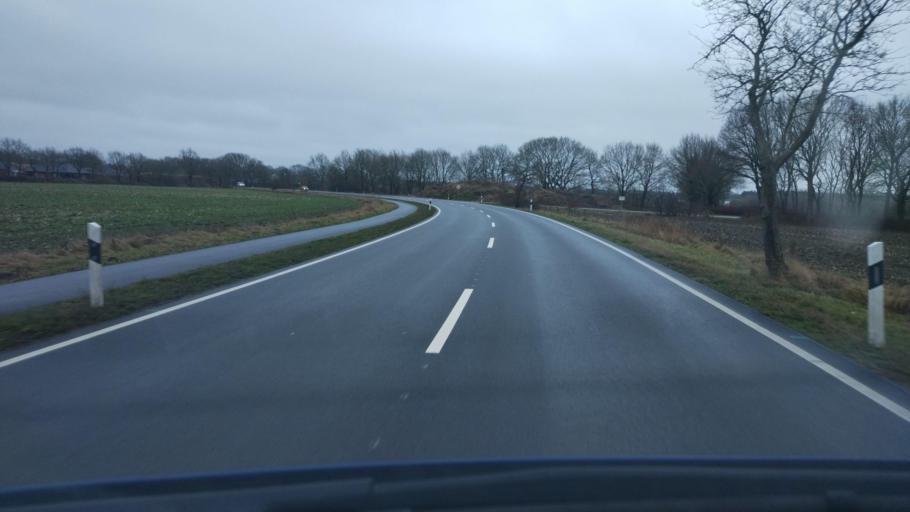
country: DE
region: Schleswig-Holstein
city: Kropp
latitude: 54.4198
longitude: 9.4935
